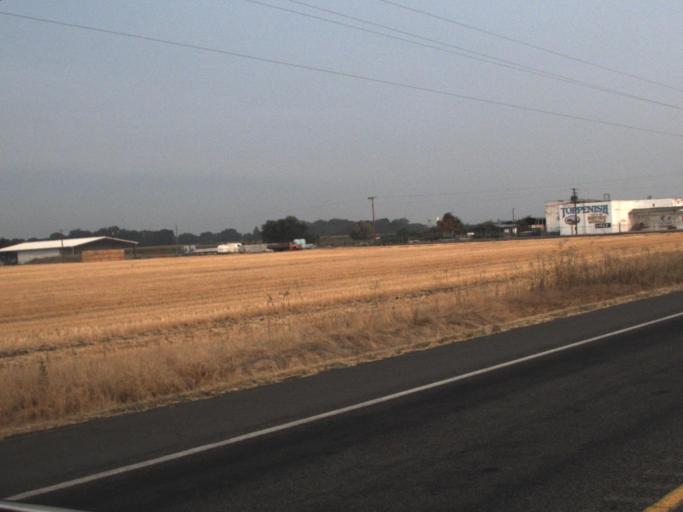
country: US
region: Washington
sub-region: Yakima County
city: Toppenish
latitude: 46.3586
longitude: -120.3202
